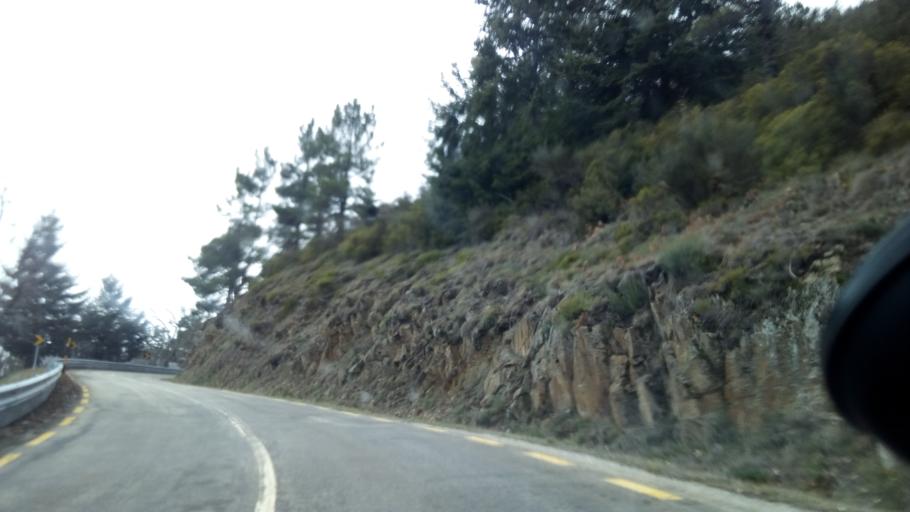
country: PT
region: Guarda
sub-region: Manteigas
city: Manteigas
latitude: 40.4173
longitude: -7.5455
